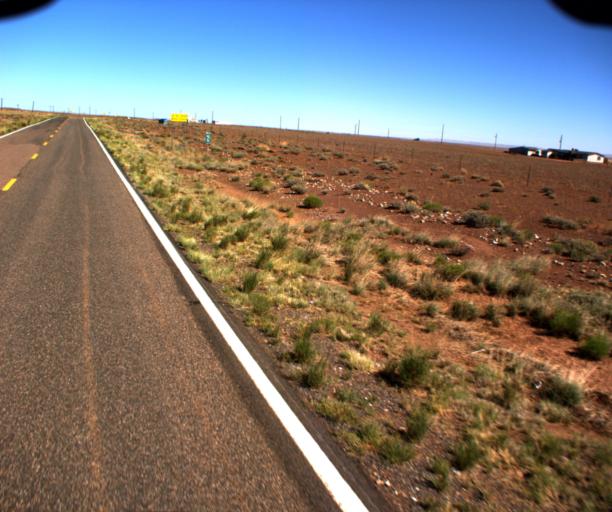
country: US
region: Arizona
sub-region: Coconino County
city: LeChee
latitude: 35.1354
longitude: -110.8859
